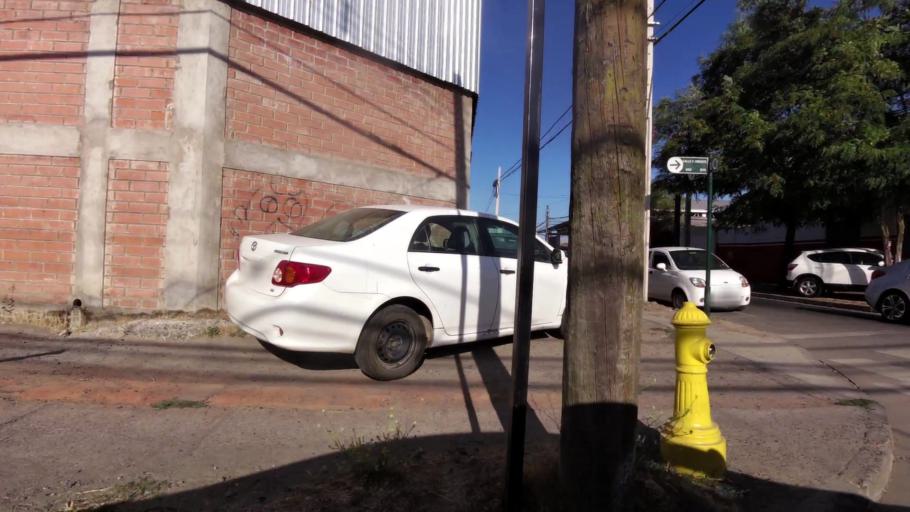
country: CL
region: Maule
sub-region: Provincia de Talca
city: Talca
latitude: -35.4301
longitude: -71.6542
